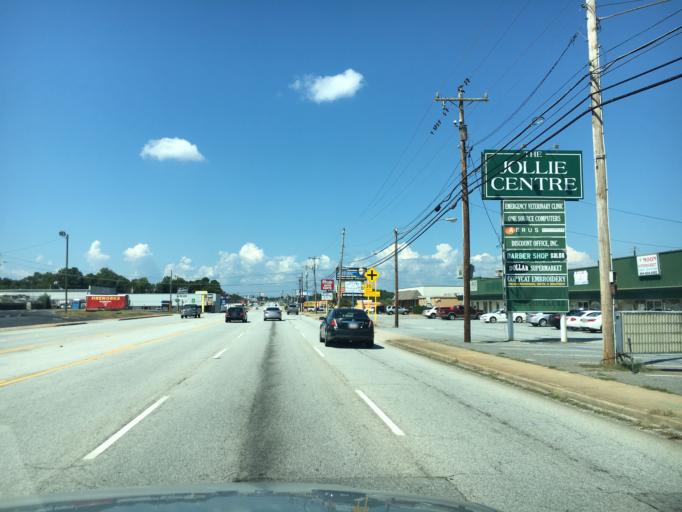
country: US
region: South Carolina
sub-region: Spartanburg County
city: Saxon
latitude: 34.9762
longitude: -81.9603
